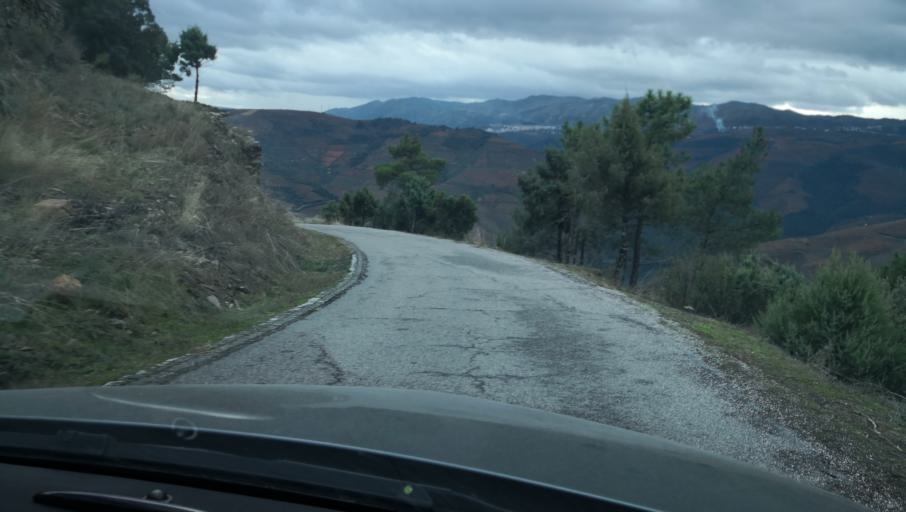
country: PT
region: Vila Real
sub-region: Sabrosa
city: Vilela
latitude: 41.1815
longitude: -7.5725
